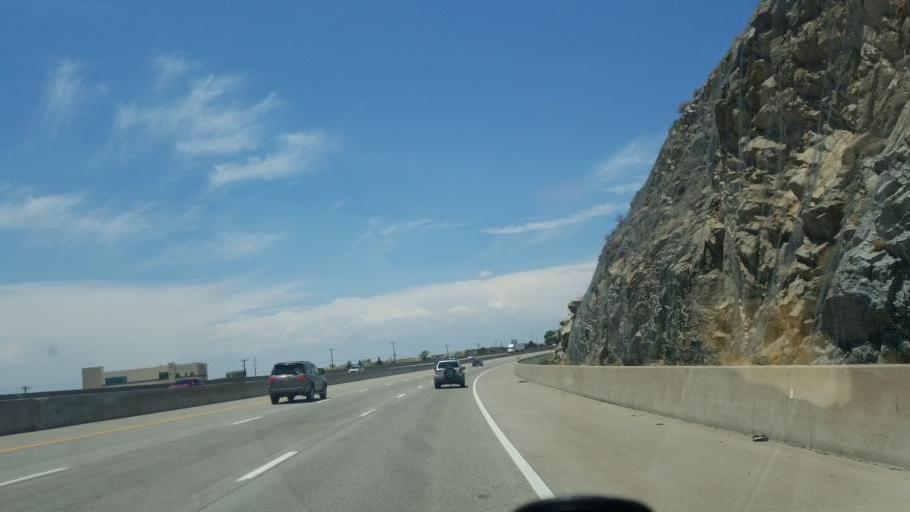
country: US
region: New Mexico
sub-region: Bernalillo County
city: Carnuel
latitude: 35.0630
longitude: -106.4804
